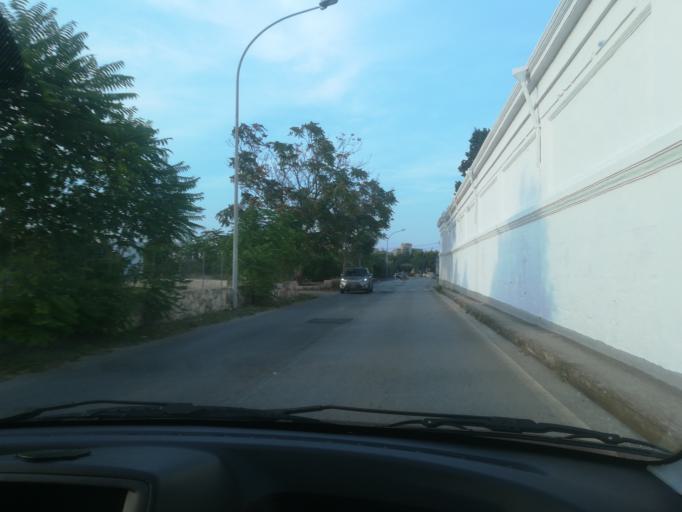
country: IT
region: Apulia
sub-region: Provincia di Bari
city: Monopoli
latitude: 40.9432
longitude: 17.2984
